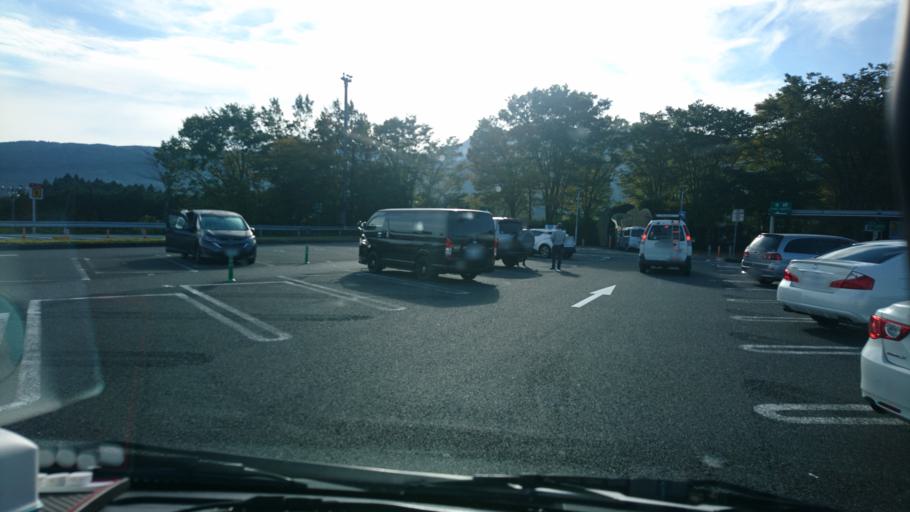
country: JP
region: Shizuoka
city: Gotemba
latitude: 35.3143
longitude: 138.9679
